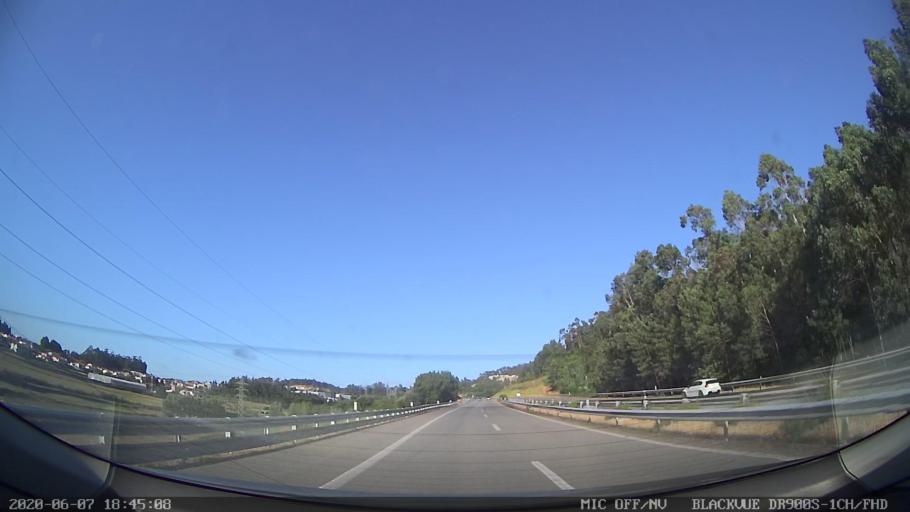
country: PT
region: Braga
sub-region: Vila Nova de Famalicao
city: Joane
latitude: 41.4064
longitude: -8.4325
